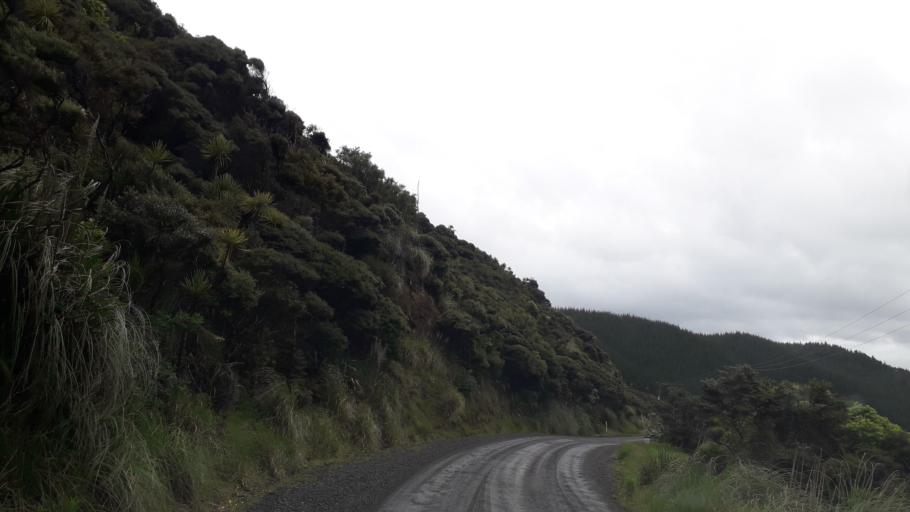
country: NZ
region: Northland
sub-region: Far North District
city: Ahipara
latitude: -35.4380
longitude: 173.3048
